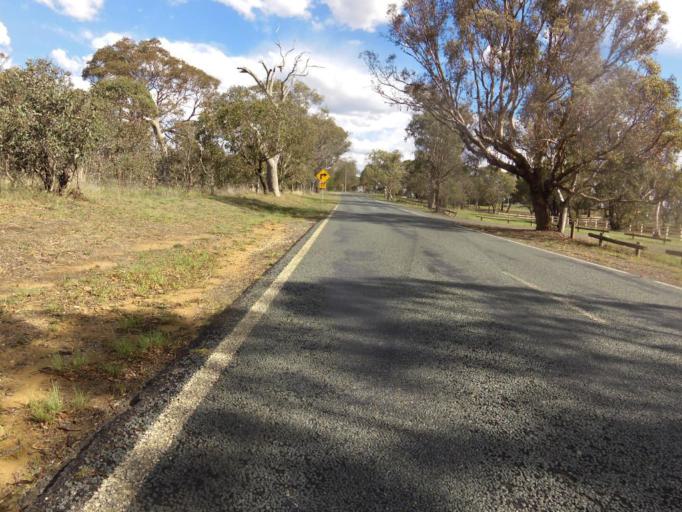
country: AU
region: Australian Capital Territory
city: Belconnen
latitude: -35.1792
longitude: 149.0731
